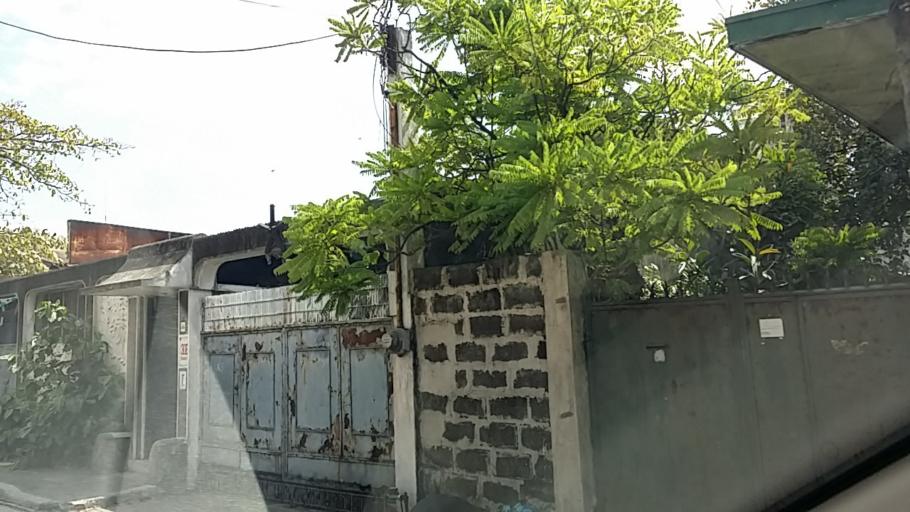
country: PH
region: Metro Manila
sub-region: Mandaluyong
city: Mandaluyong City
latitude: 14.5774
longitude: 121.0457
